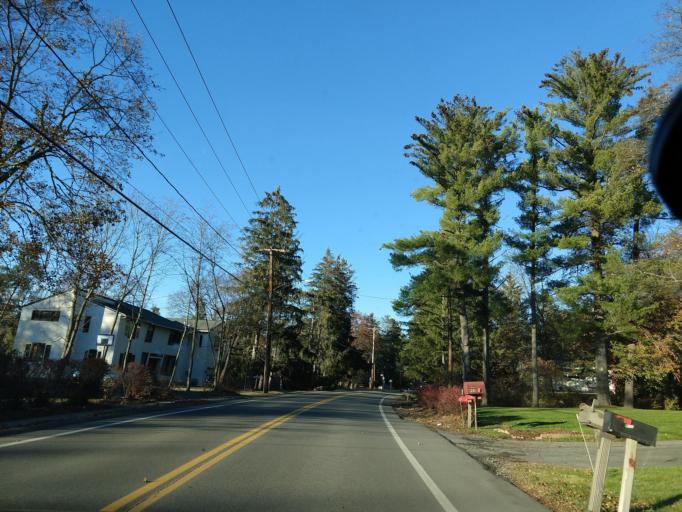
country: US
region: New York
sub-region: Tompkins County
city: Cayuga Heights
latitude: 42.4652
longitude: -76.4842
